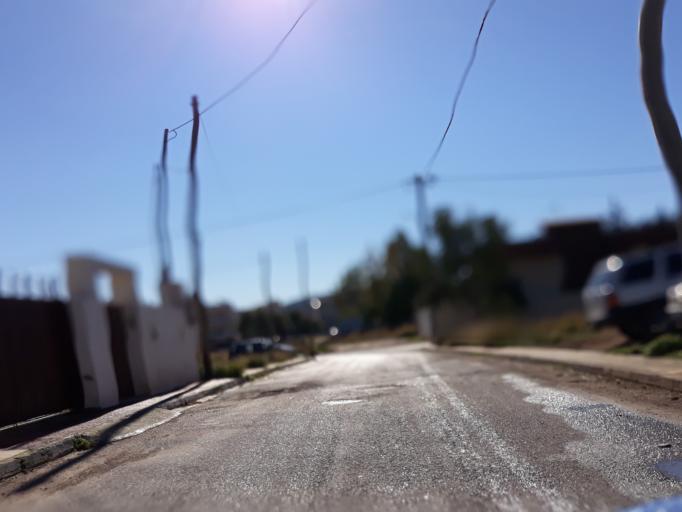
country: GR
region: Attica
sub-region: Nomarchia Dytikis Attikis
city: Ano Liosia
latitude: 38.0918
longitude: 23.7092
